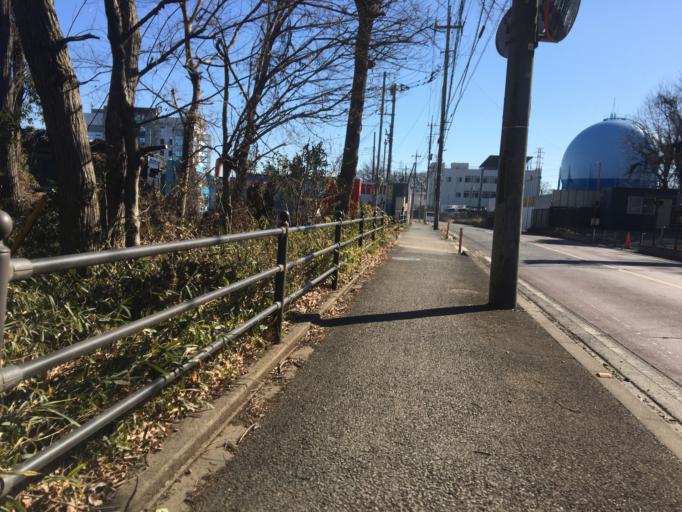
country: JP
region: Saitama
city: Oi
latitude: 35.8298
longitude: 139.5244
